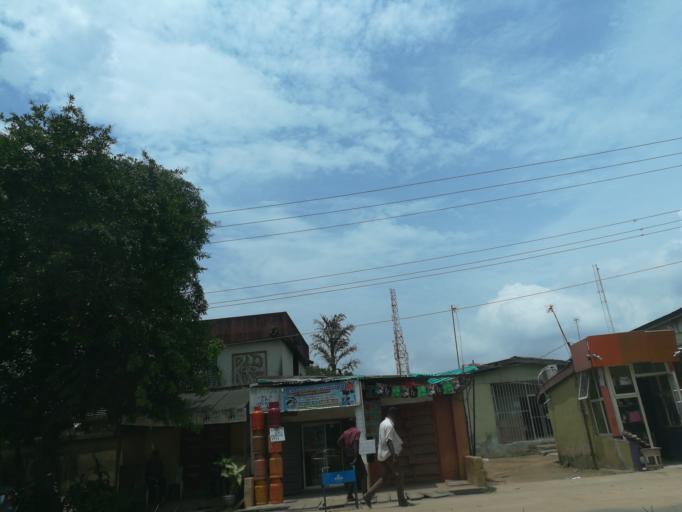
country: NG
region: Lagos
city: Oshodi
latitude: 6.5473
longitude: 3.3287
